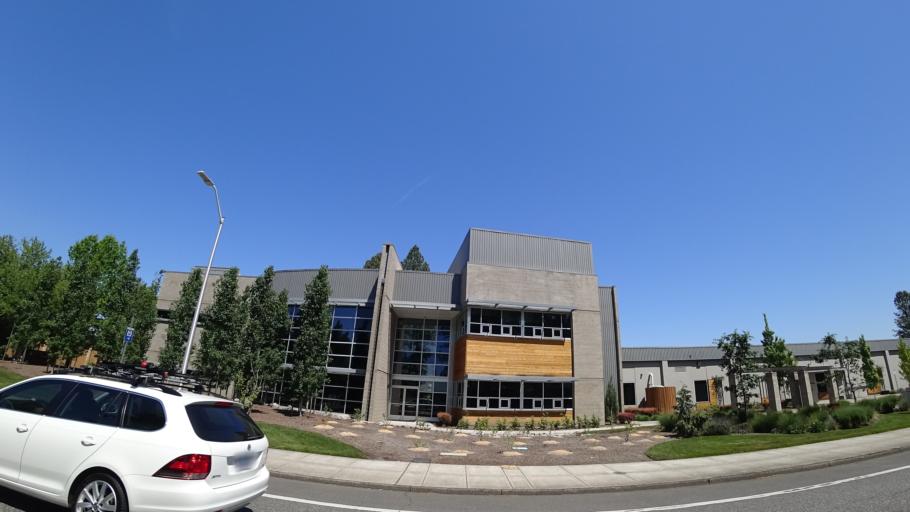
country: US
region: Oregon
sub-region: Washington County
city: Beaverton
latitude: 45.4932
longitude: -122.8213
